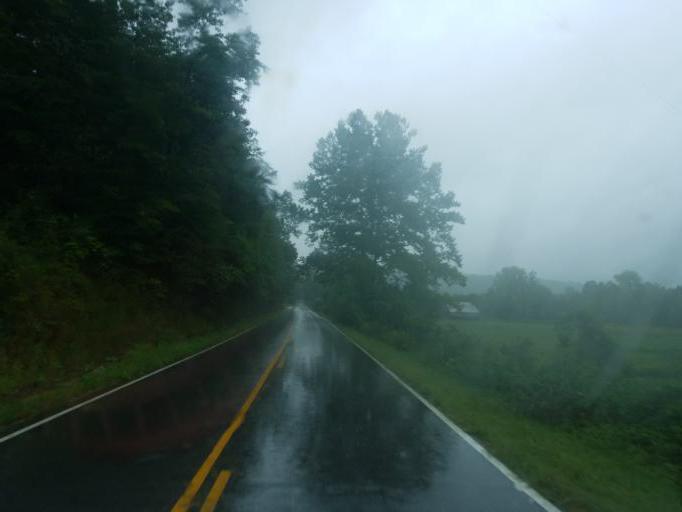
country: US
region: Kentucky
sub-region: Carter County
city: Grayson
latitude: 38.4782
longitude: -83.0324
